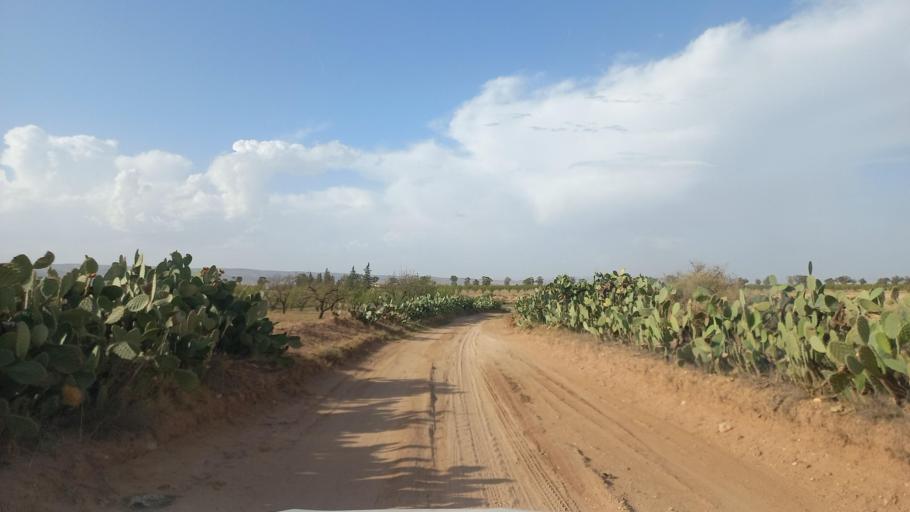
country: TN
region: Al Qasrayn
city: Kasserine
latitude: 35.2271
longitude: 8.9678
